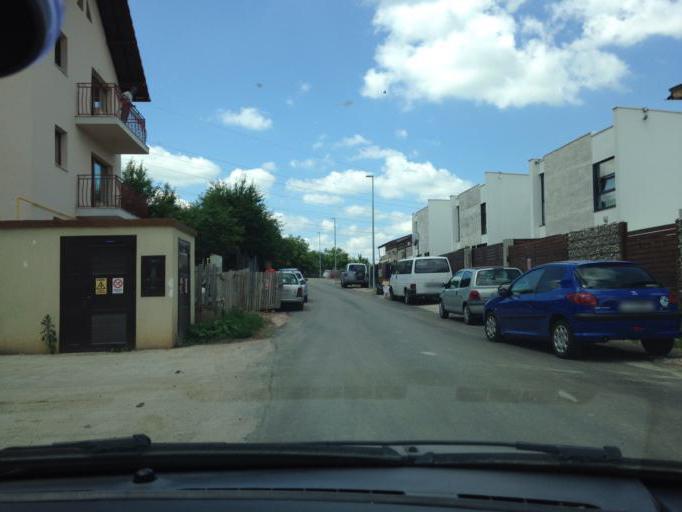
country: RO
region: Cluj
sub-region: Comuna Floresti
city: Floresti
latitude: 46.7465
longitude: 23.5284
